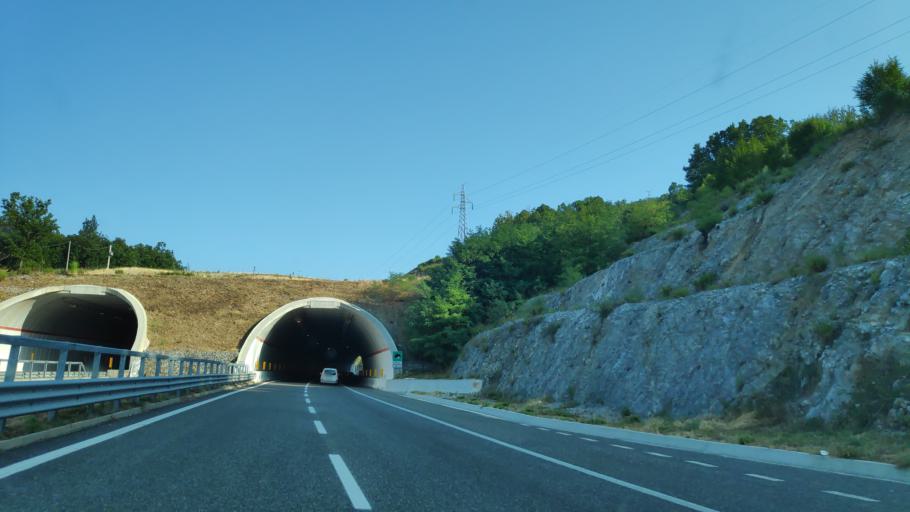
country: IT
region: Basilicate
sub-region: Provincia di Potenza
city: Lauria
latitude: 40.0283
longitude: 15.8758
